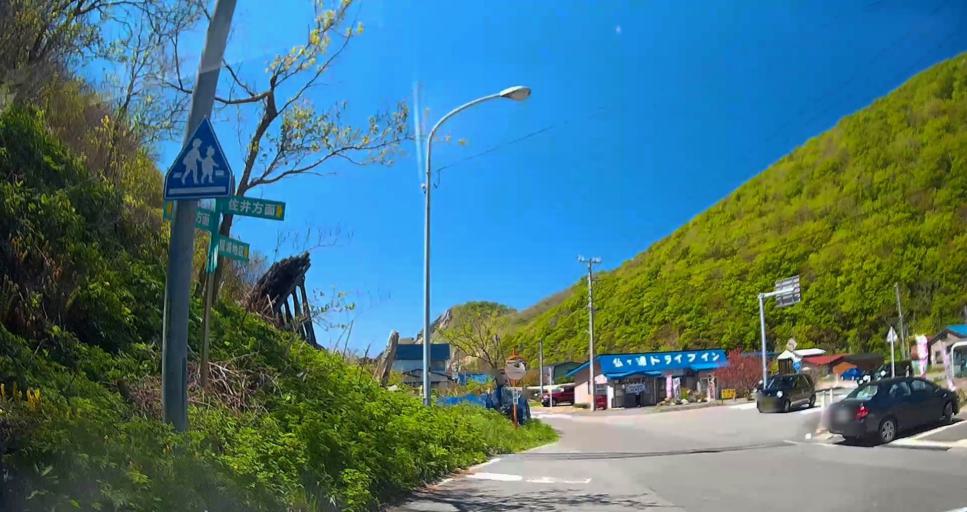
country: JP
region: Aomori
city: Mutsu
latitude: 41.3274
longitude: 140.8122
